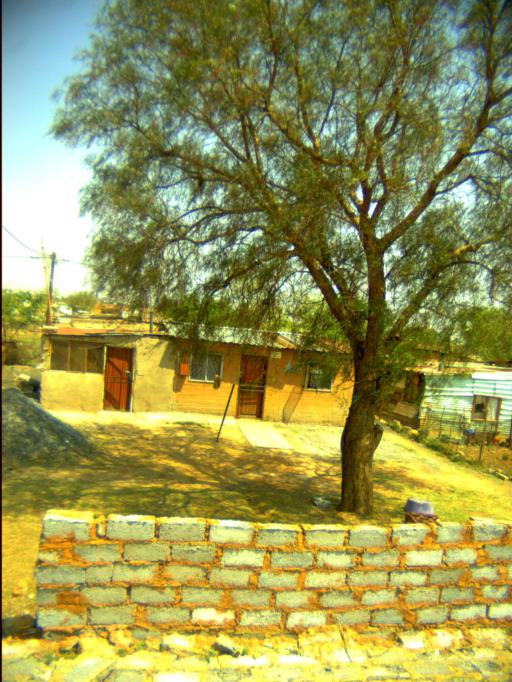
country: ZA
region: Mpumalanga
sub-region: Nkangala District Municipality
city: Delmas
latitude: -26.1390
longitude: 28.6979
